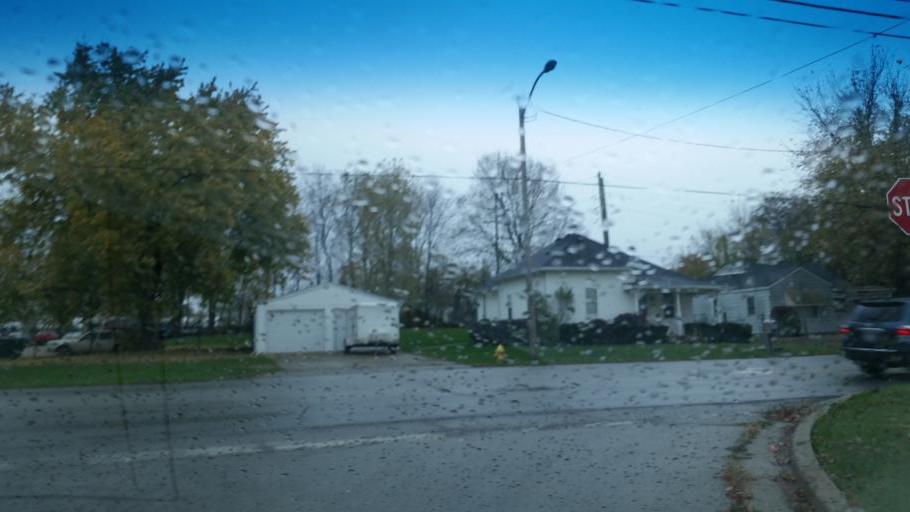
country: US
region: Indiana
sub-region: Howard County
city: Kokomo
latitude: 40.4762
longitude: -86.1539
